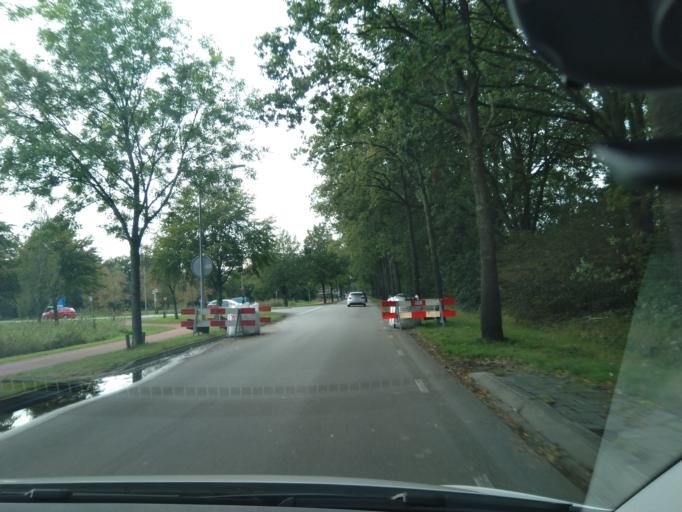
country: NL
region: Groningen
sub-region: Gemeente Veendam
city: Veendam
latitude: 53.0956
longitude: 6.9146
